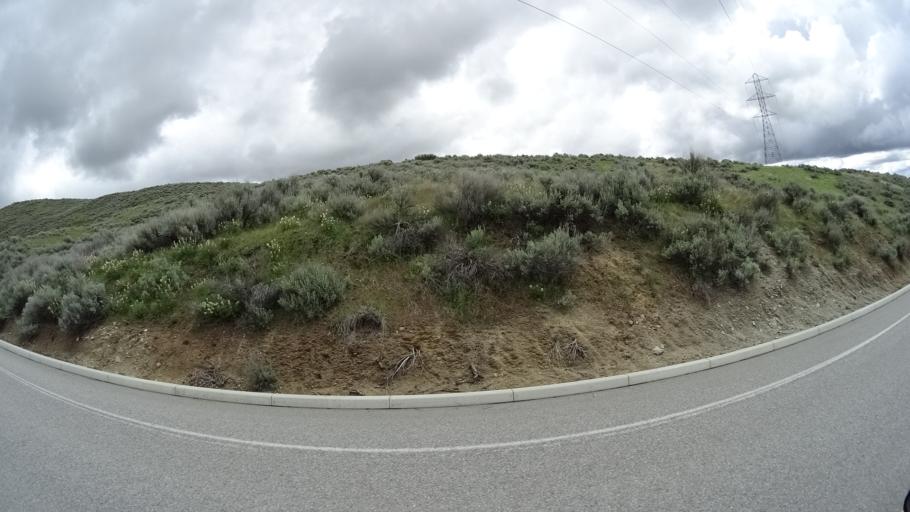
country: US
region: Idaho
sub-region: Ada County
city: Boise
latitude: 43.6996
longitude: -116.1685
